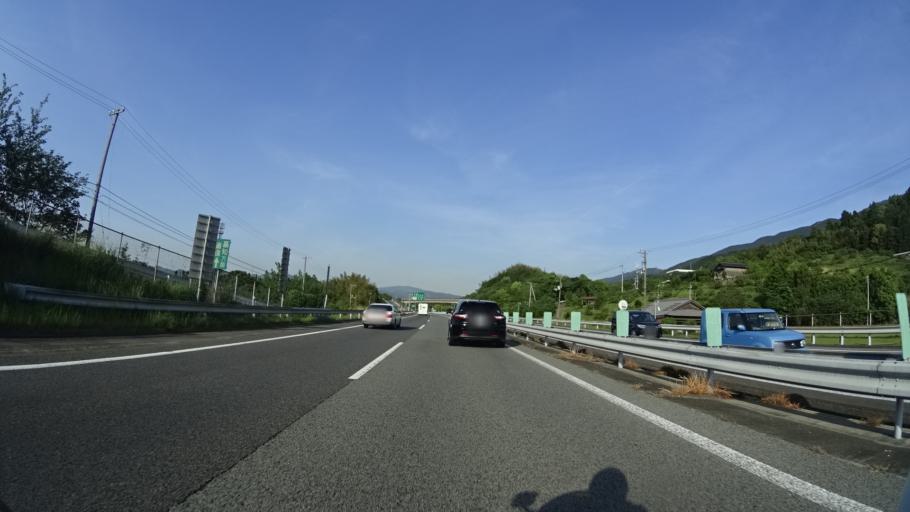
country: JP
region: Ehime
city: Kawanoecho
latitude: 33.9764
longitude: 133.5711
